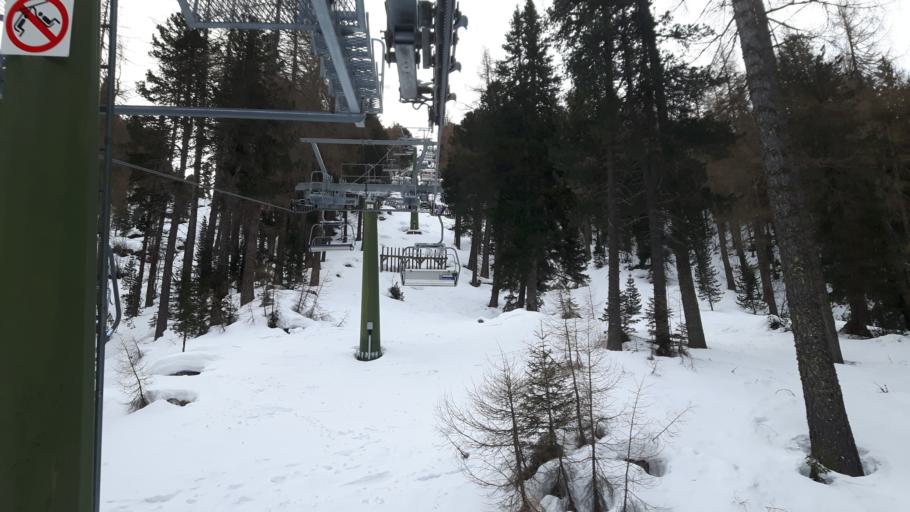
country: IT
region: Trentino-Alto Adige
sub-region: Provincia di Trento
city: Panchia
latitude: 46.3399
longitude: 11.5427
